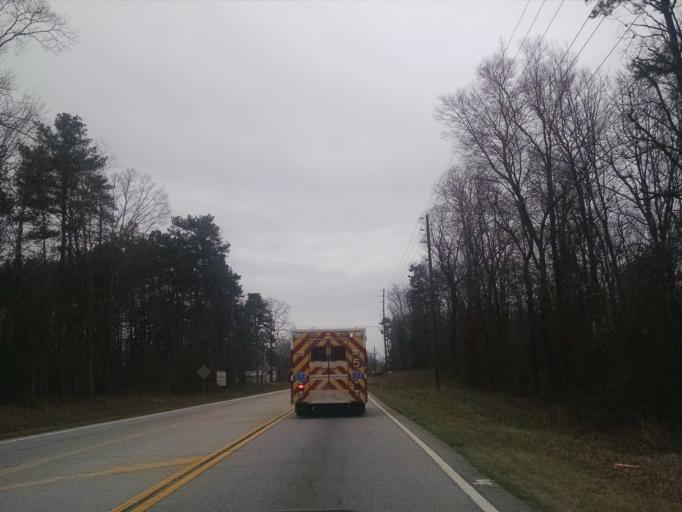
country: US
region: Georgia
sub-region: Hall County
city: Oakwood
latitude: 34.1978
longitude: -83.8876
